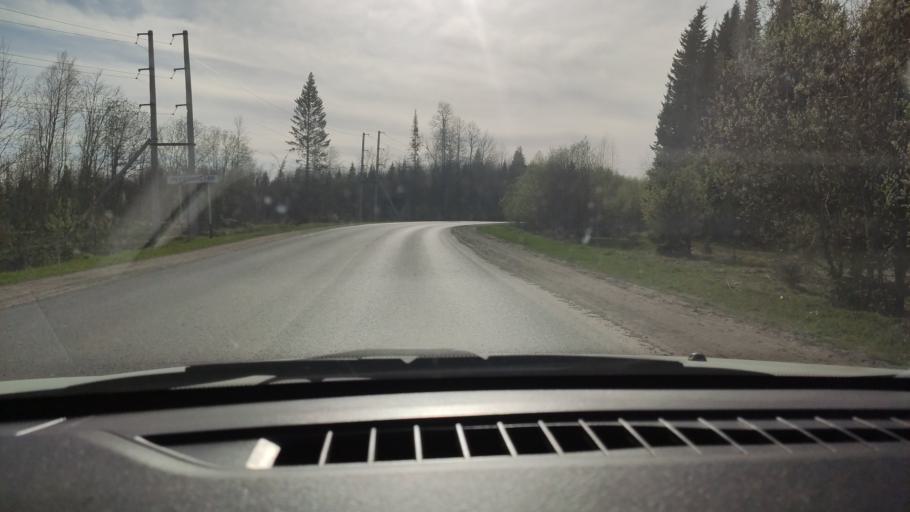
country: RU
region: Perm
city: Novyye Lyady
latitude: 57.9424
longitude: 56.5692
